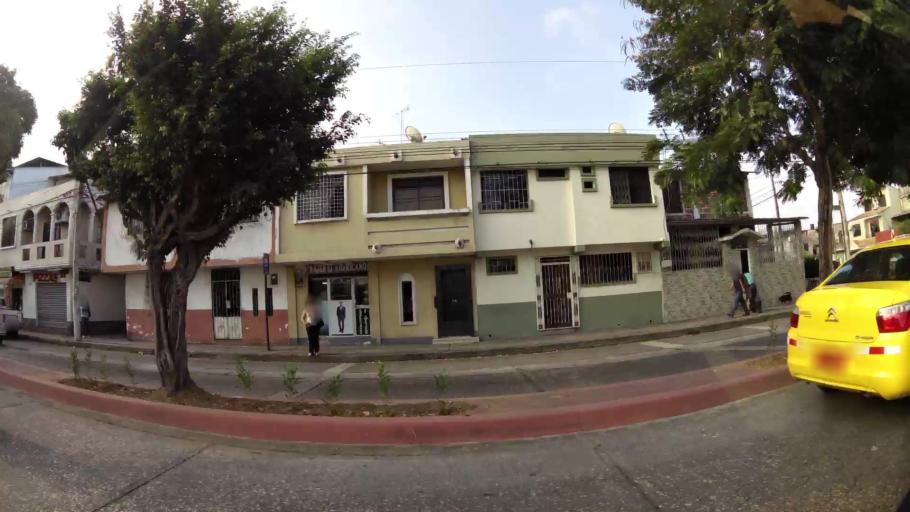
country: EC
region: Guayas
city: Eloy Alfaro
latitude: -2.1299
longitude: -79.9048
